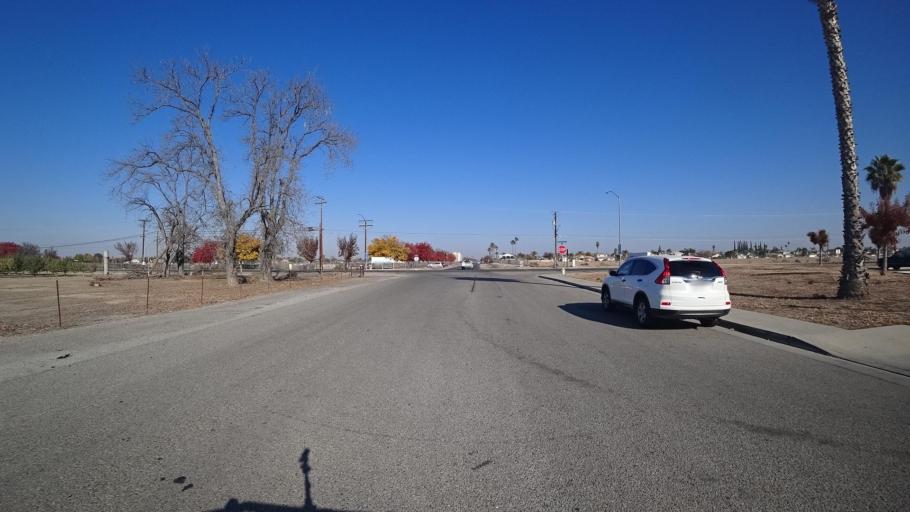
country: US
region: California
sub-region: Kern County
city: Delano
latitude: 35.7609
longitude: -119.2320
